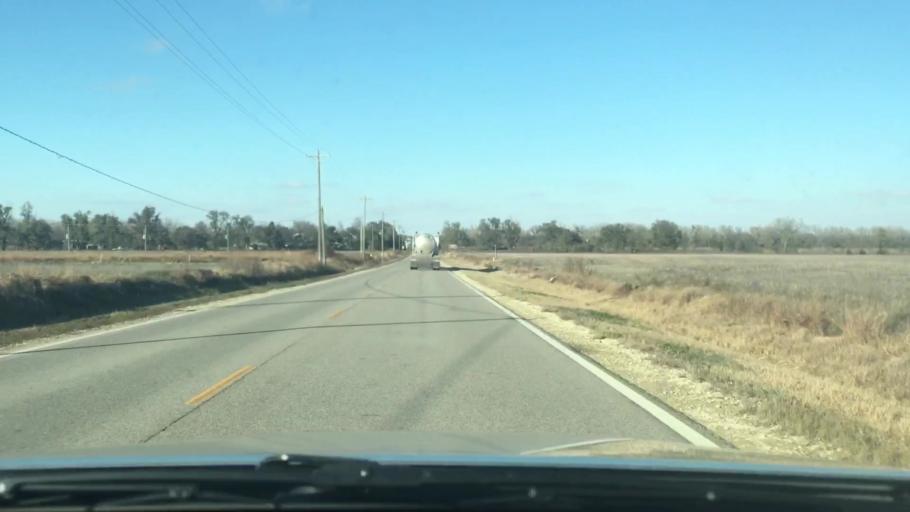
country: US
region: Kansas
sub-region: Rice County
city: Sterling
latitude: 38.1632
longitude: -98.2067
